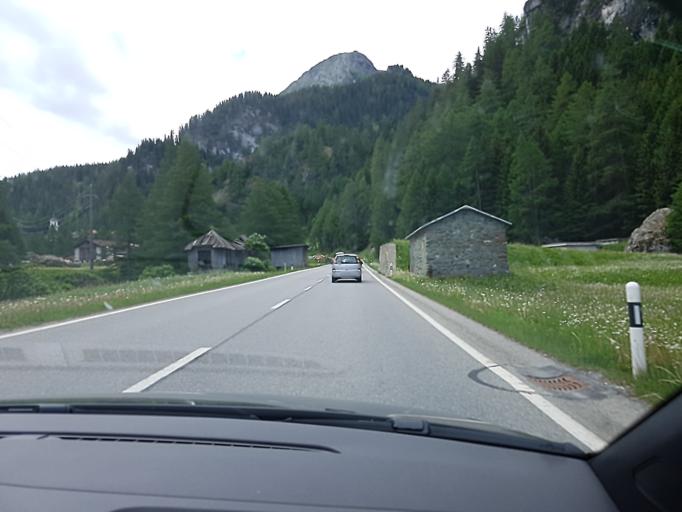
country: CH
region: Grisons
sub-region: Albula District
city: Tiefencastel
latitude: 46.5286
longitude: 9.6206
